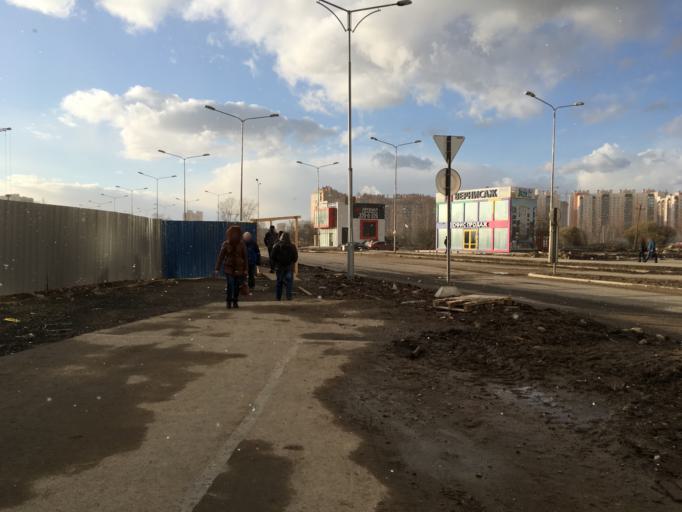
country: RU
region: Leningrad
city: Rybatskoye
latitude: 59.9085
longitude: 30.5127
